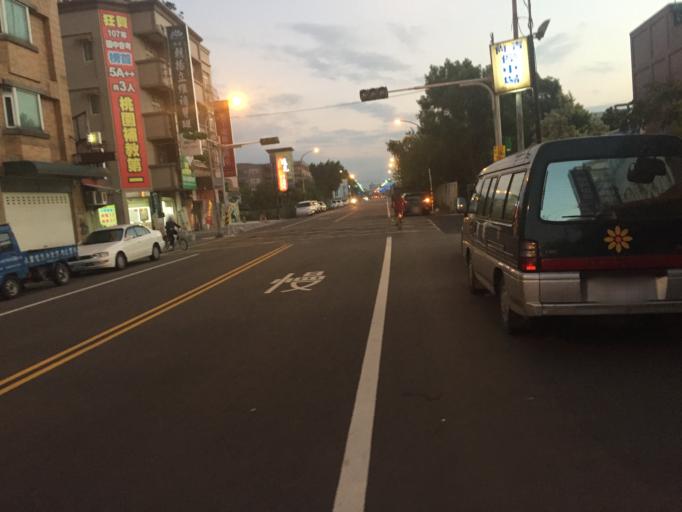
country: TW
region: Taiwan
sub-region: Taoyuan
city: Taoyuan
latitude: 24.9792
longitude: 121.3146
